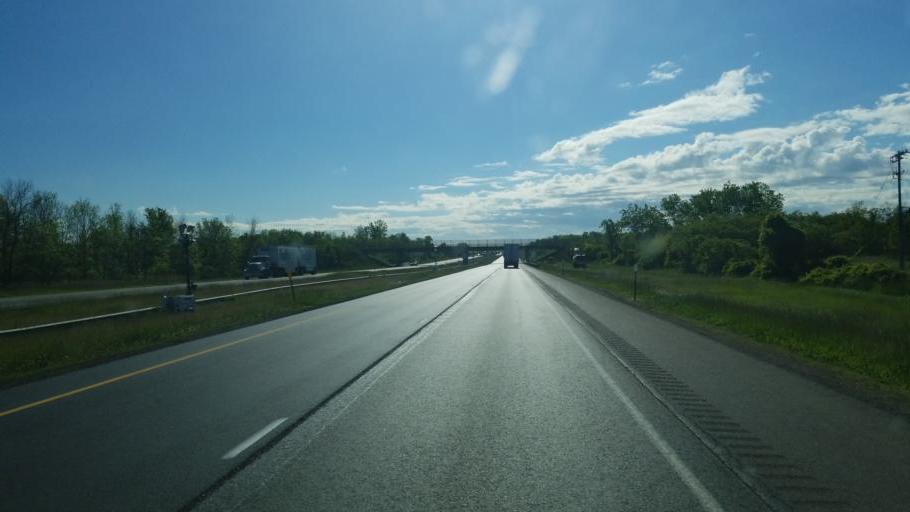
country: US
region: New York
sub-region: Livingston County
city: Caledonia
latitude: 43.0298
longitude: -77.8801
